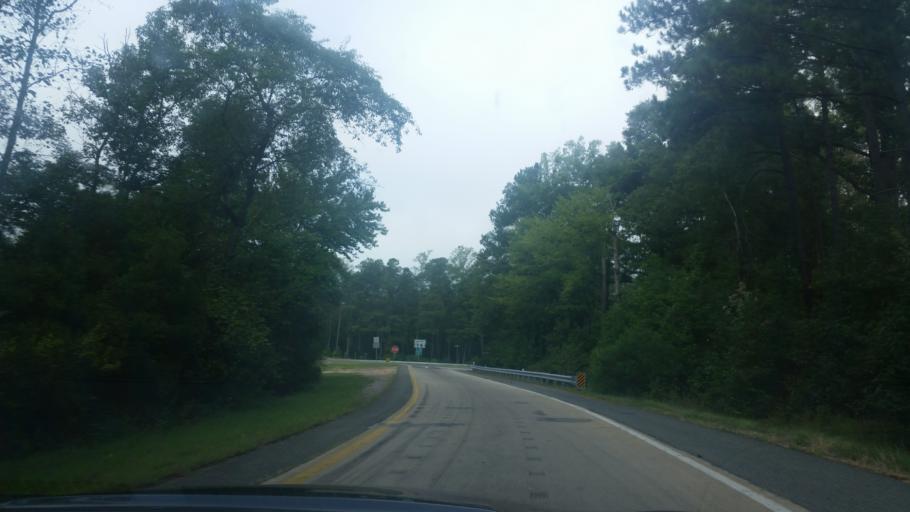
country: US
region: Virginia
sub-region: Henrico County
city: Sandston
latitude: 37.5175
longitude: -77.1875
